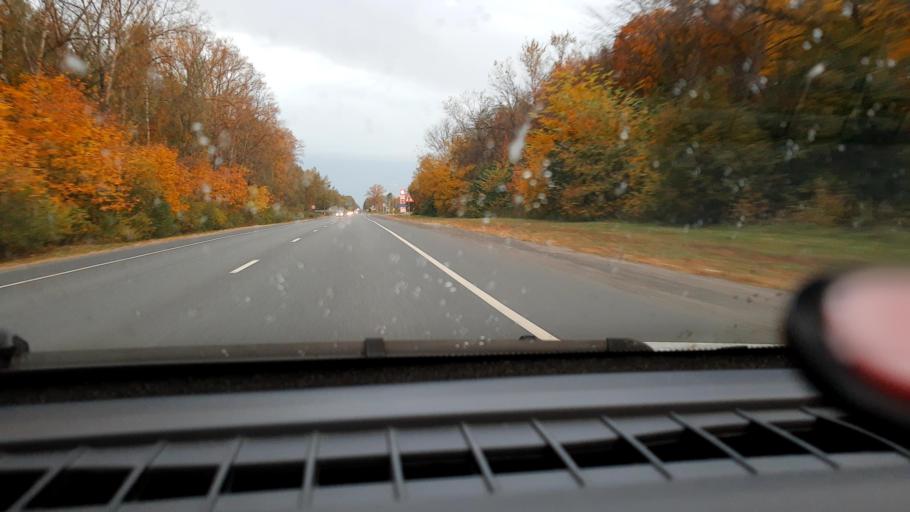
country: RU
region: Vladimir
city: Orgtrud
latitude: 56.2028
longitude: 40.7647
